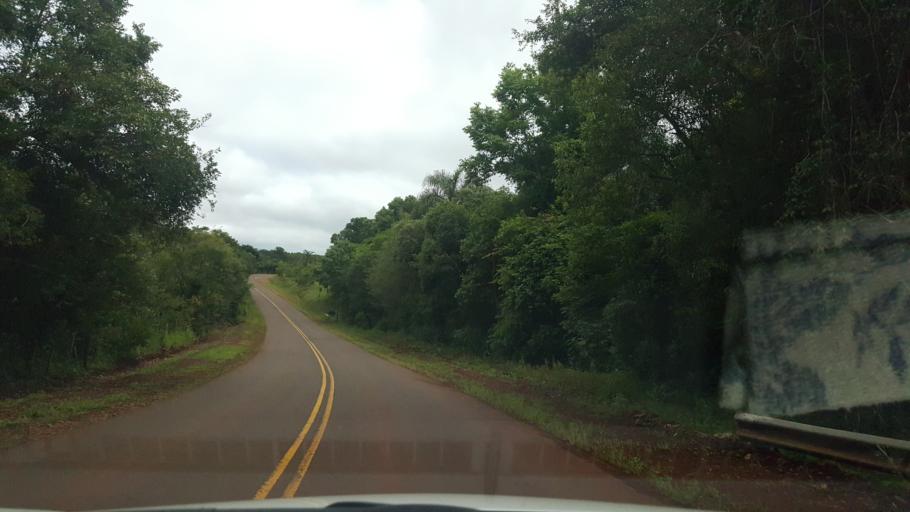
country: AR
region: Misiones
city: Capiovi
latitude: -26.9558
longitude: -55.0921
